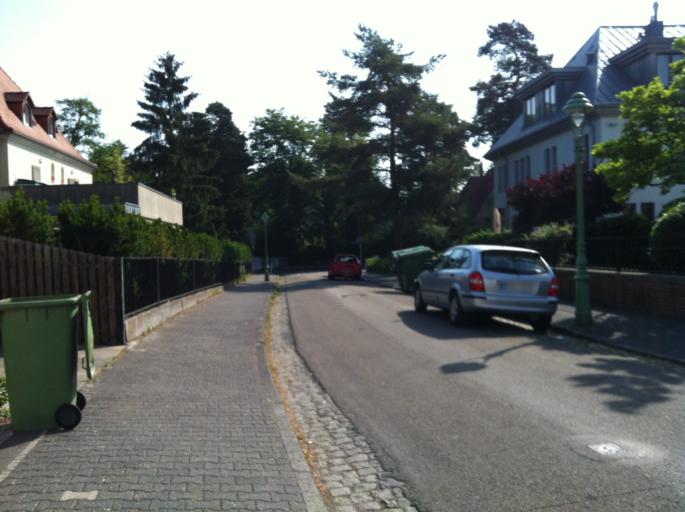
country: DE
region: Rheinland-Pfalz
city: Budenheim
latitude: 50.0040
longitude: 8.2008
